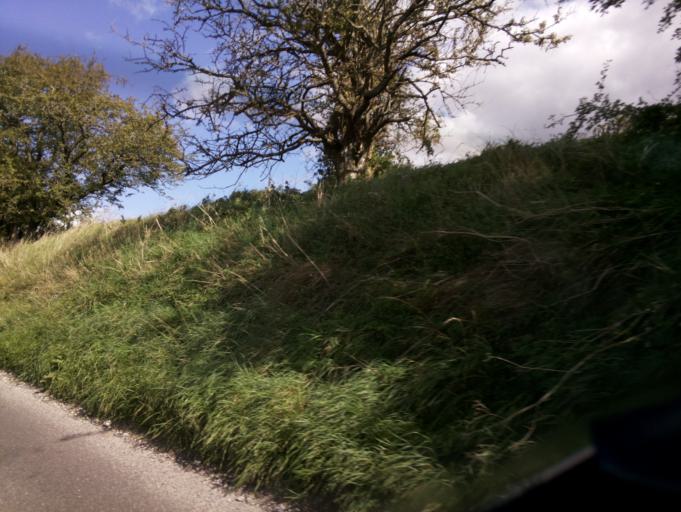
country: GB
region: England
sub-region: Wiltshire
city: Stockton
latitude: 51.2081
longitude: -2.0001
